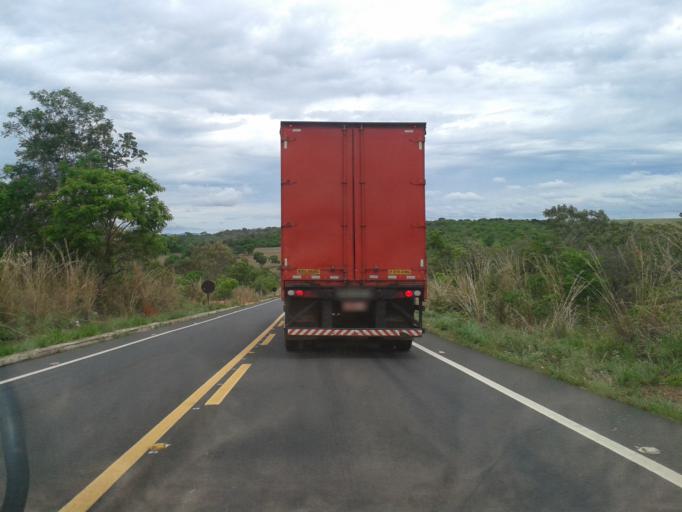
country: BR
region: Goias
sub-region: Caldas Novas
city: Caldas Novas
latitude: -17.8508
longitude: -48.6376
